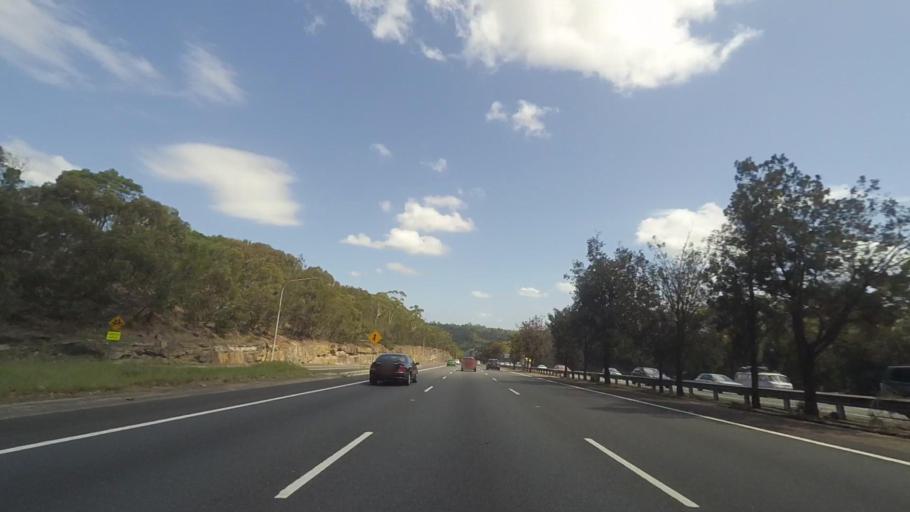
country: AU
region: New South Wales
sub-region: Hornsby Shire
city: Mount Colah
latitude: -33.6826
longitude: 151.1206
